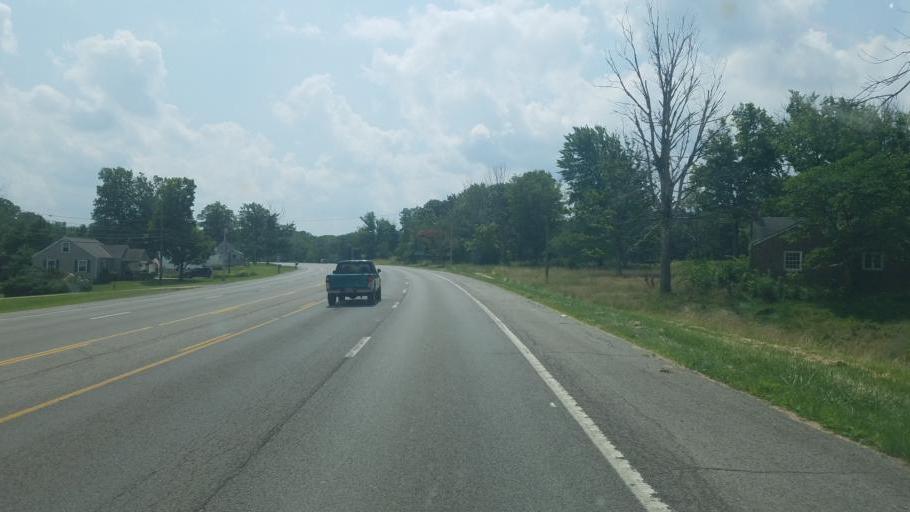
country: US
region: Ohio
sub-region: Richland County
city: Ontario
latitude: 40.8073
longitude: -82.5888
